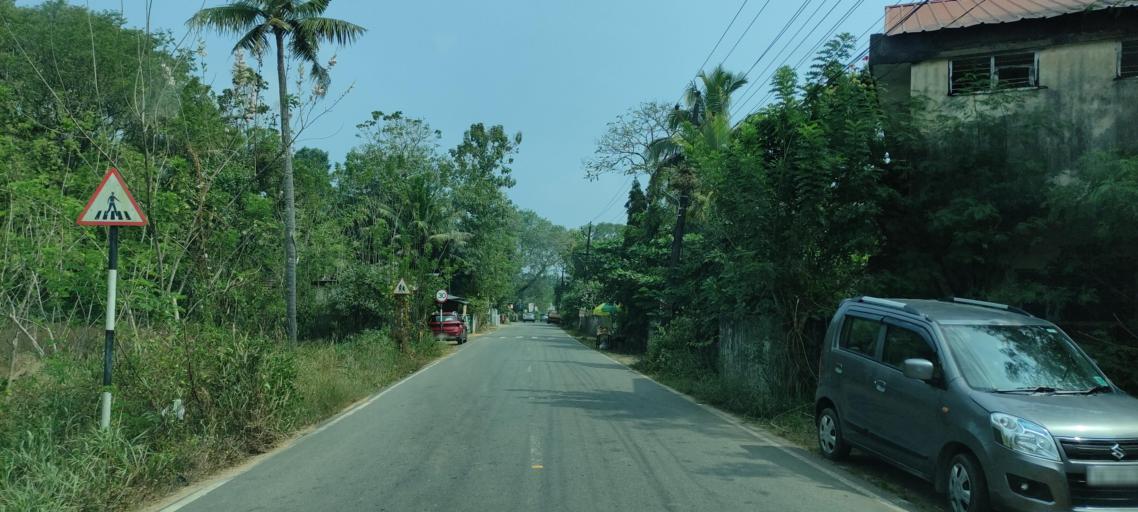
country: IN
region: Kerala
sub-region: Alappuzha
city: Shertallai
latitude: 9.6551
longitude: 76.3501
